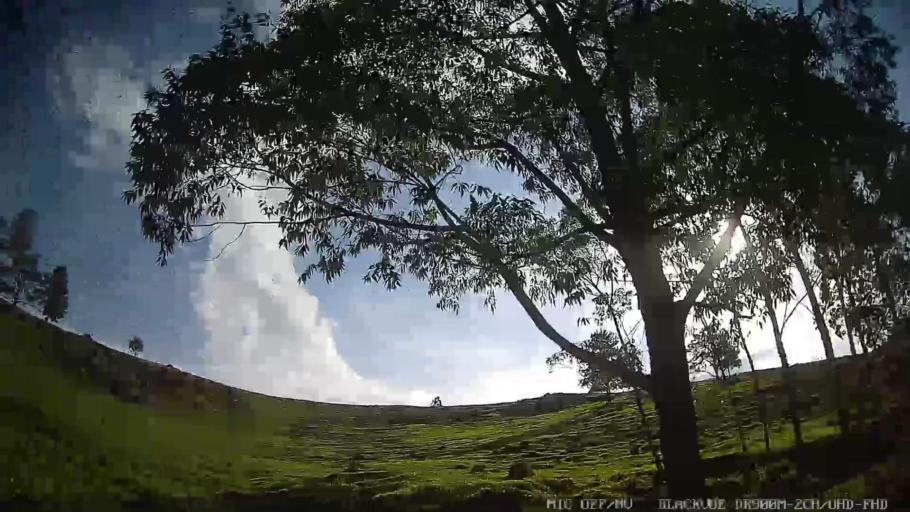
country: BR
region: Sao Paulo
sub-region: Serra Negra
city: Serra Negra
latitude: -22.6485
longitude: -46.6959
